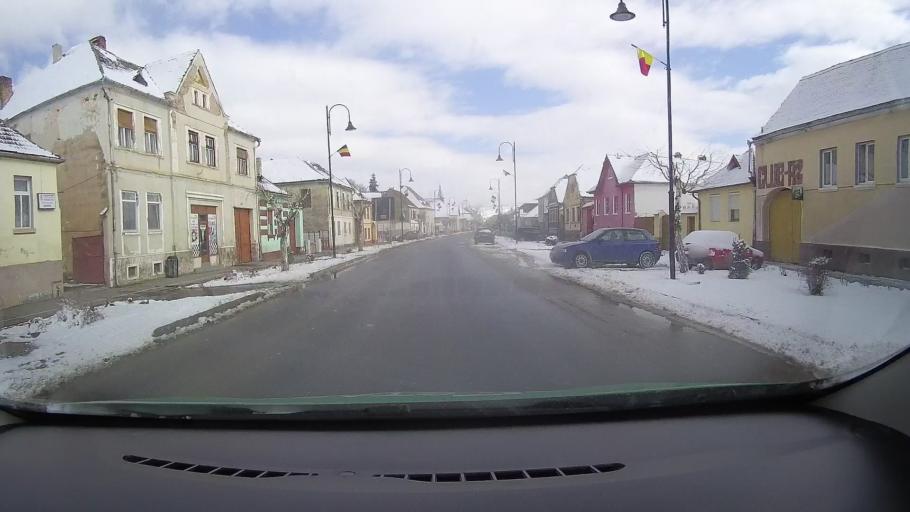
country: RO
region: Sibiu
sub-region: Oras Agnita
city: Agnita
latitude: 45.9761
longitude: 24.6164
